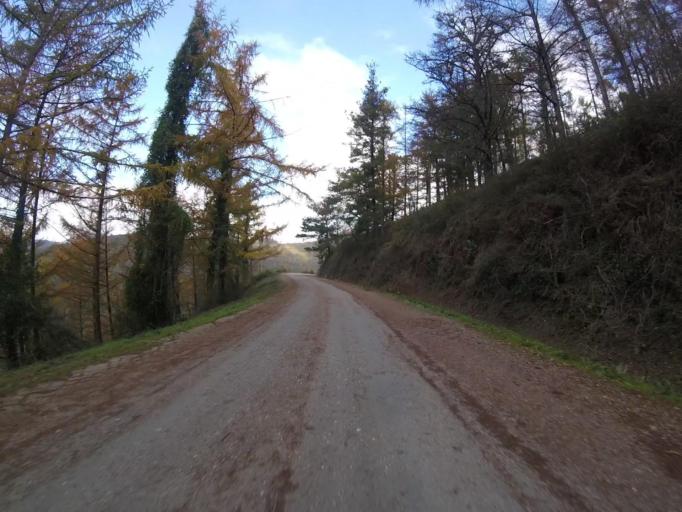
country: ES
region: Navarre
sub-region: Provincia de Navarra
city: Goizueta
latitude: 43.2166
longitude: -1.8516
